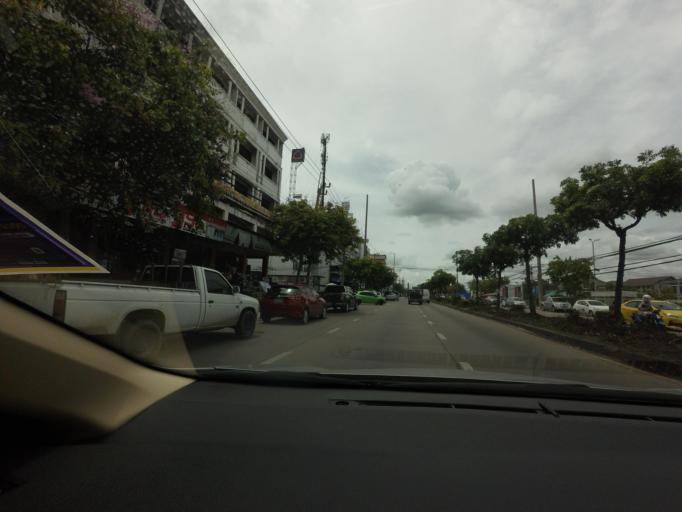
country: TH
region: Bangkok
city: Lat Krabang
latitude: 13.7209
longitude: 100.7933
